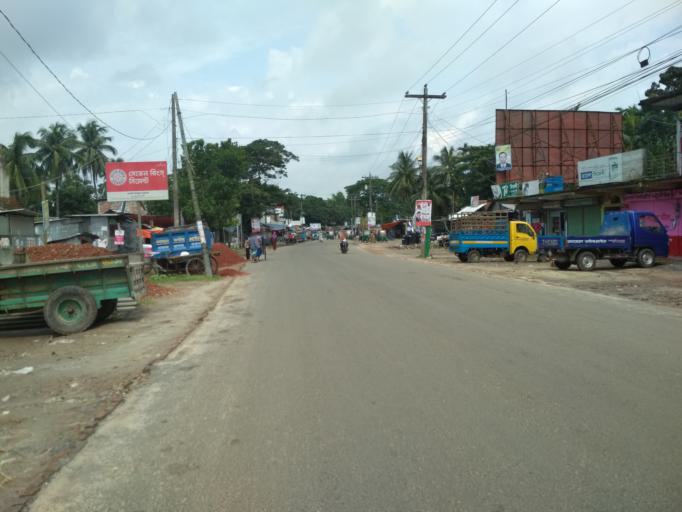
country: BD
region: Chittagong
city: Lakshmipur
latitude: 22.9691
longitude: 90.8072
